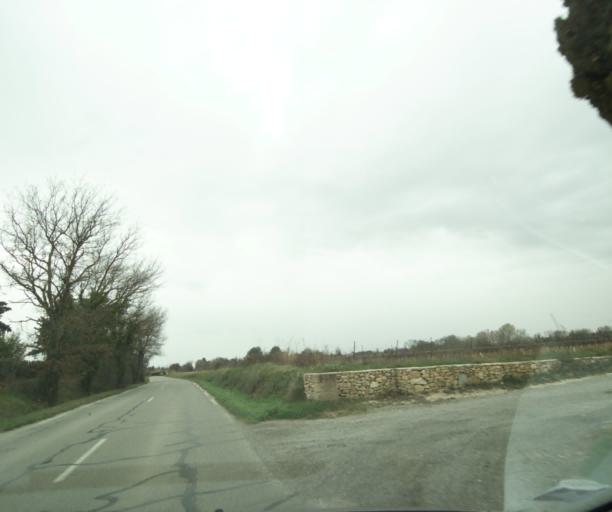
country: FR
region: Provence-Alpes-Cote d'Azur
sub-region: Departement des Bouches-du-Rhone
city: Venelles
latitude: 43.5798
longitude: 5.4539
